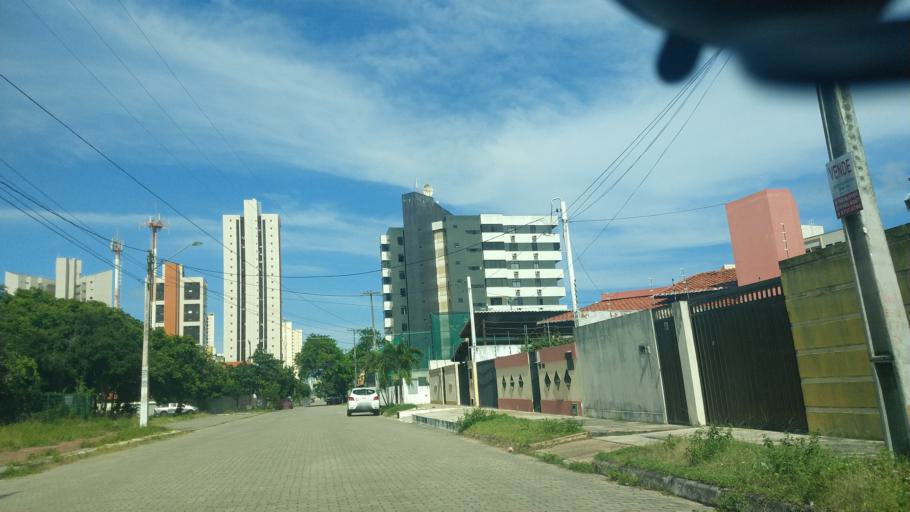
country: BR
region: Rio Grande do Norte
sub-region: Natal
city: Natal
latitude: -5.8612
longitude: -35.1982
